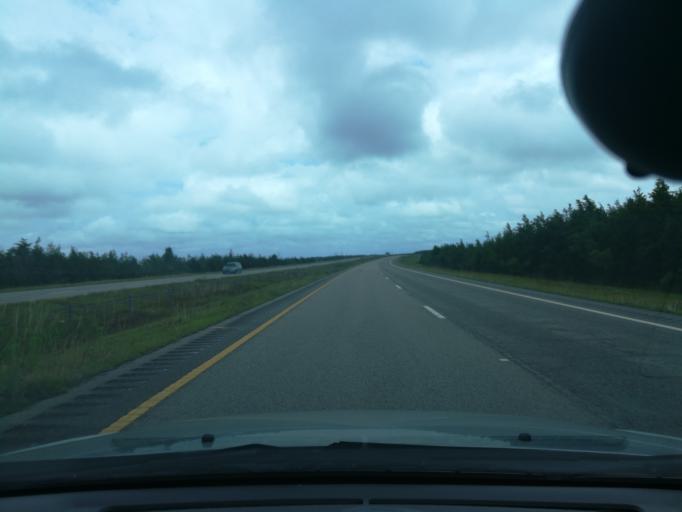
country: US
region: North Carolina
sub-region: Chowan County
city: Edenton
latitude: 35.9057
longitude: -76.4897
